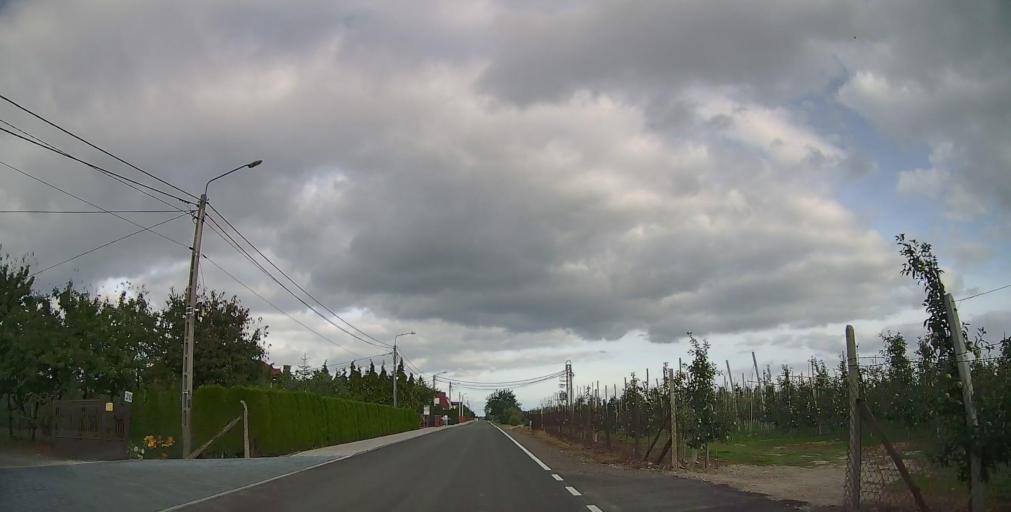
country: PL
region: Masovian Voivodeship
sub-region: Powiat bialobrzeski
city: Promna
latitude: 51.7088
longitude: 20.9398
